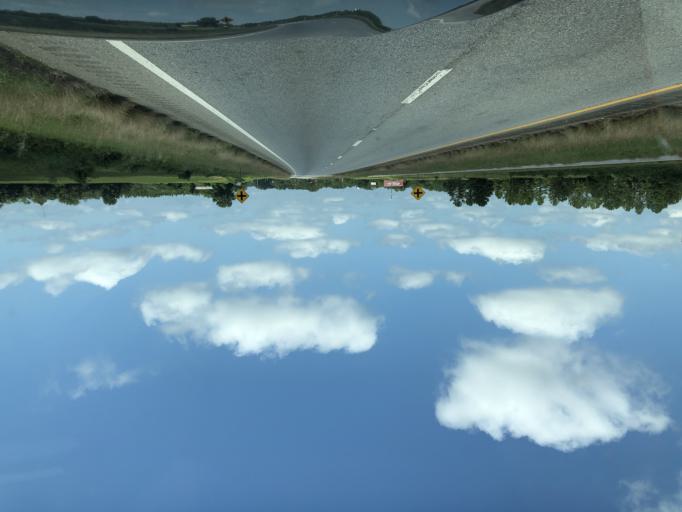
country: US
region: Alabama
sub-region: Henry County
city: Abbeville
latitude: 31.5336
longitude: -85.2908
